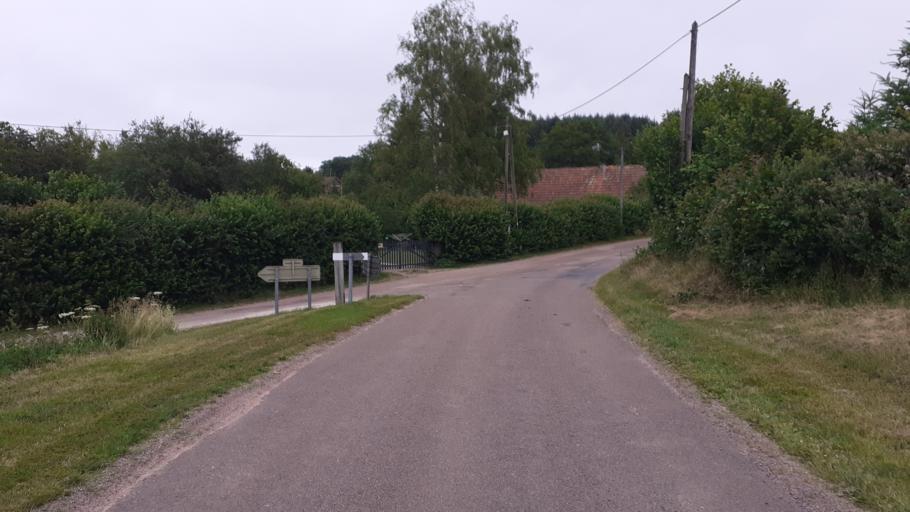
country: FR
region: Bourgogne
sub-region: Departement de la Cote-d'Or
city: Saulieu
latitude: 47.2751
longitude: 4.1417
